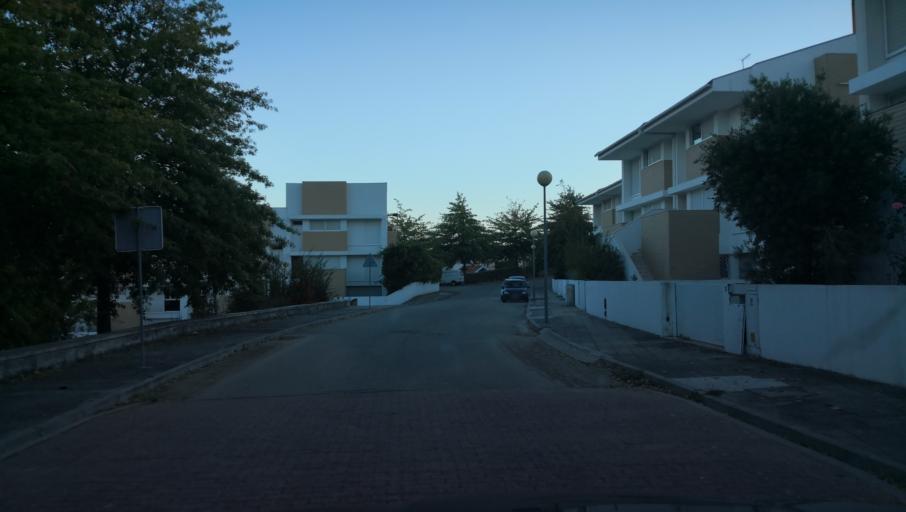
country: PT
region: Vila Real
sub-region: Vila Real
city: Vila Real
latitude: 41.3080
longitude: -7.7663
